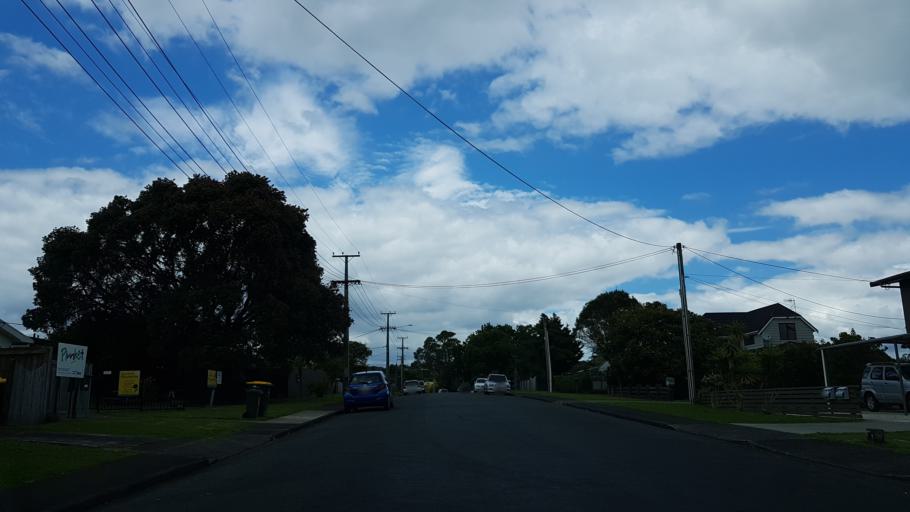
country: NZ
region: Auckland
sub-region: Auckland
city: North Shore
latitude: -36.7931
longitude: 174.6866
